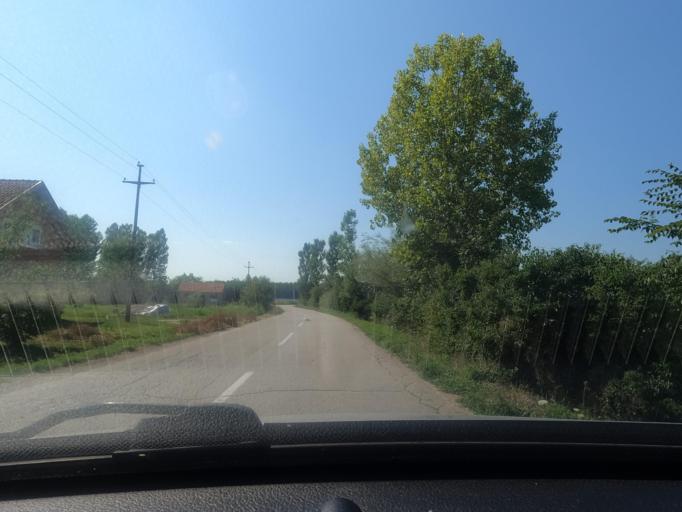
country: RS
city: Kozjak
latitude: 44.5718
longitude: 19.2833
